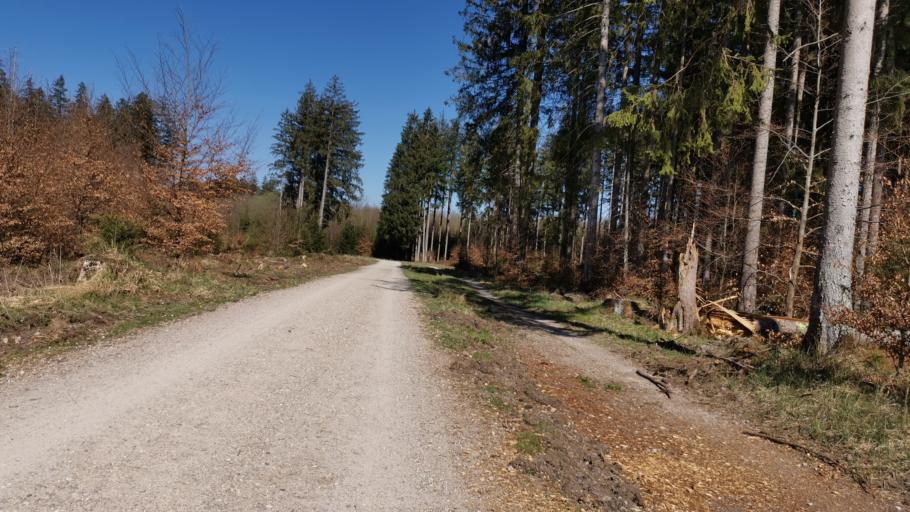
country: DE
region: Bavaria
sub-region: Upper Bavaria
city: Pullach im Isartal
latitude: 48.0692
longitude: 11.4988
